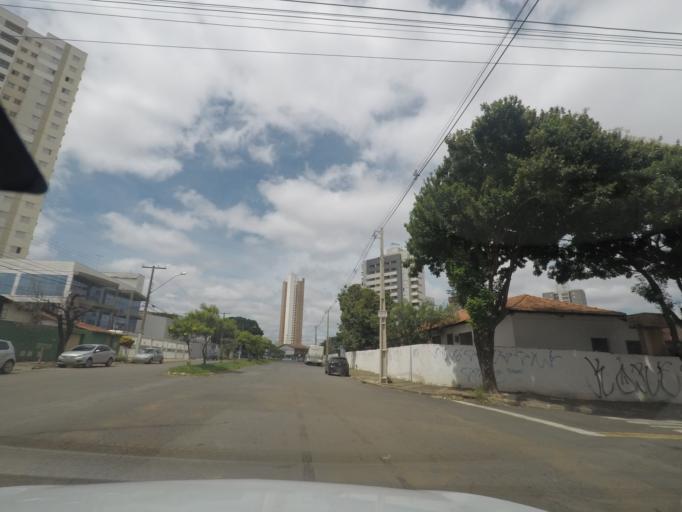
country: BR
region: Goias
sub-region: Goiania
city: Goiania
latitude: -16.6778
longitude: -49.2384
